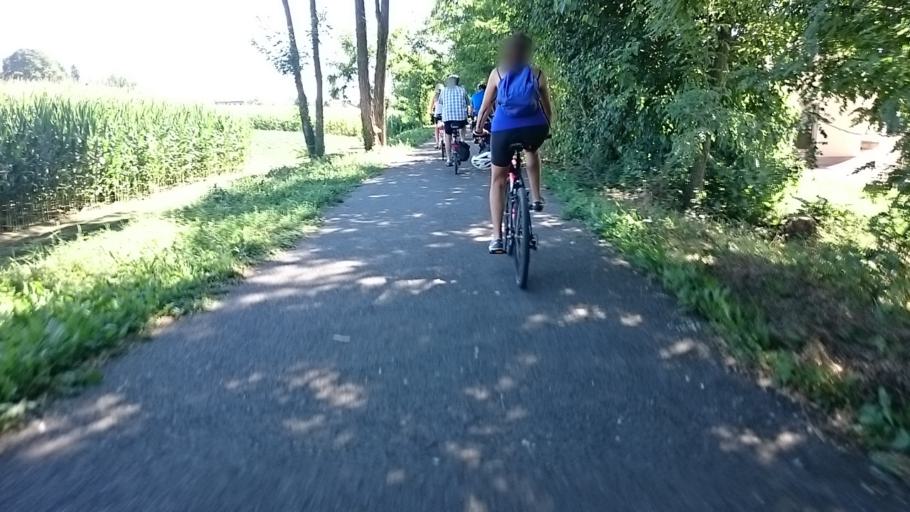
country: IT
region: Veneto
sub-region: Provincia di Padova
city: Loreggia
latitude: 45.5908
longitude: 11.9683
